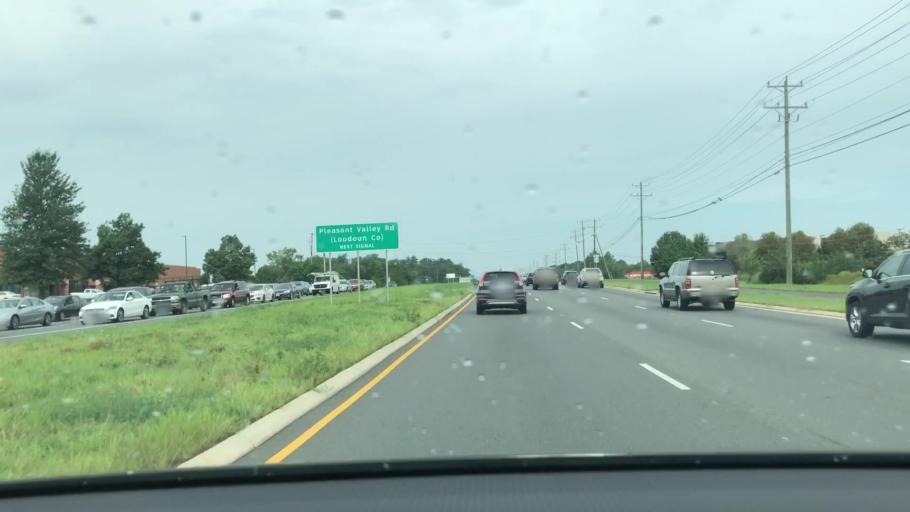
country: US
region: Virginia
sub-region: Loudoun County
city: South Riding
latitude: 38.9107
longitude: -77.4713
